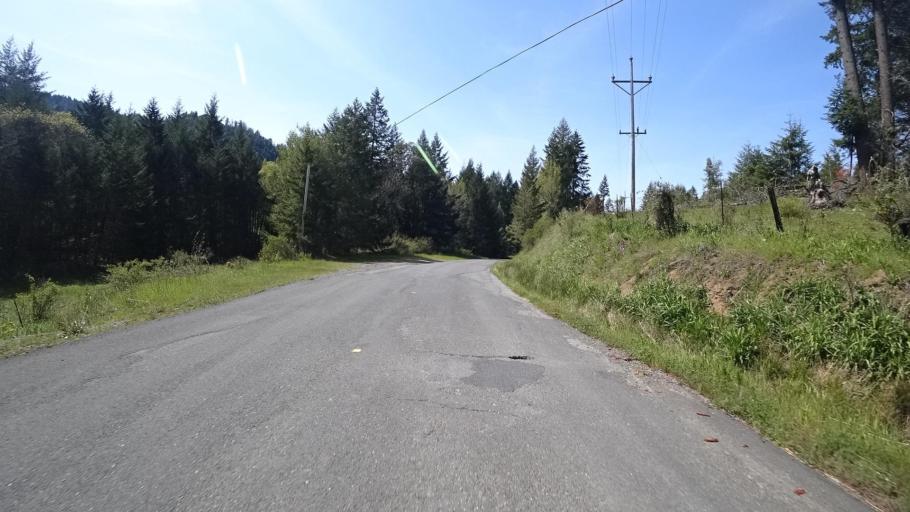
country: US
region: California
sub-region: Humboldt County
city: Redway
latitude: 40.3738
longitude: -123.7384
